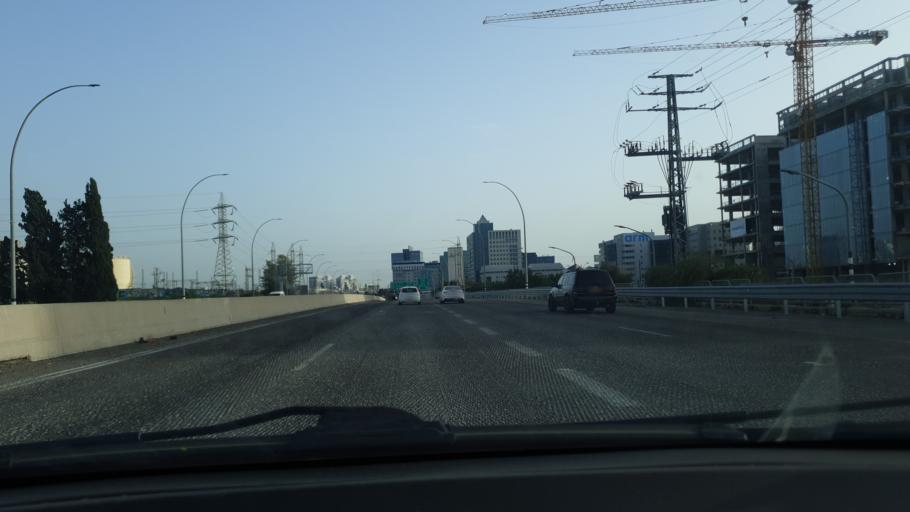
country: IL
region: Central District
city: Ra'anana
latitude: 32.2022
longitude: 34.8844
